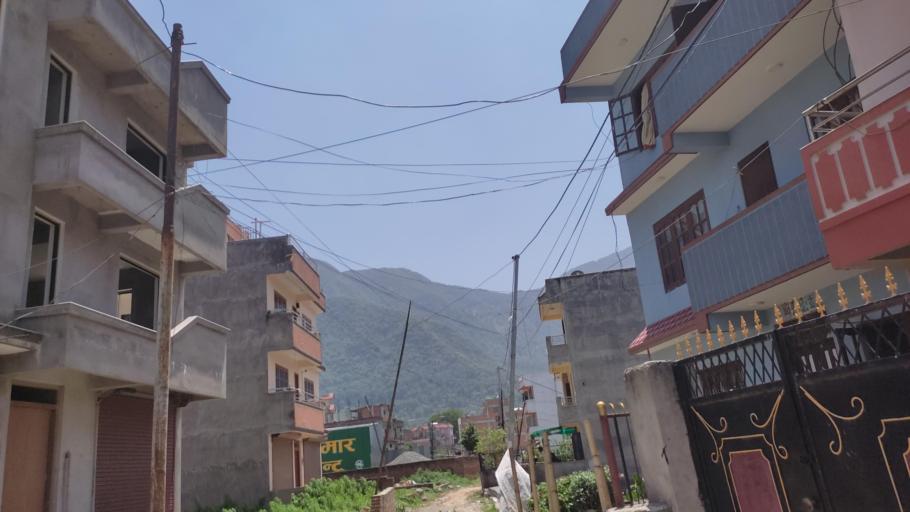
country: NP
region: Central Region
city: Kirtipur
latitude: 27.6685
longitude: 85.2676
